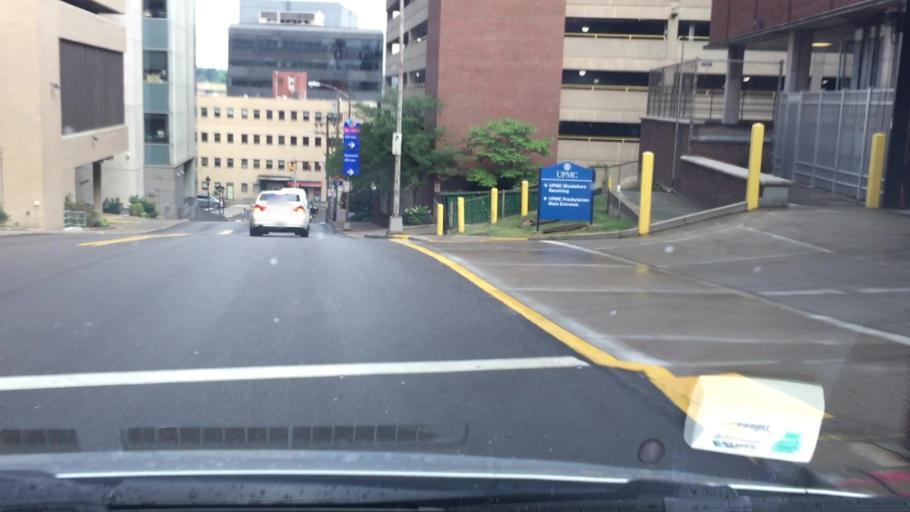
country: US
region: Pennsylvania
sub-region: Allegheny County
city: Bloomfield
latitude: 40.4412
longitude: -79.9614
